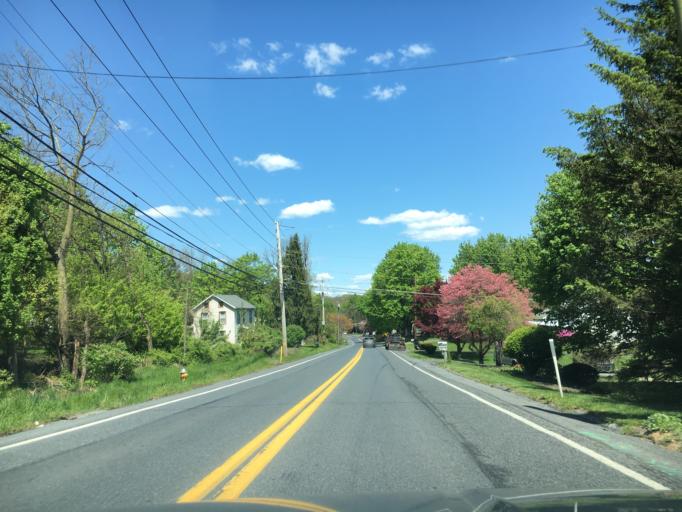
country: US
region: Pennsylvania
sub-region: Lehigh County
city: Allentown
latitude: 40.6240
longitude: -75.5078
